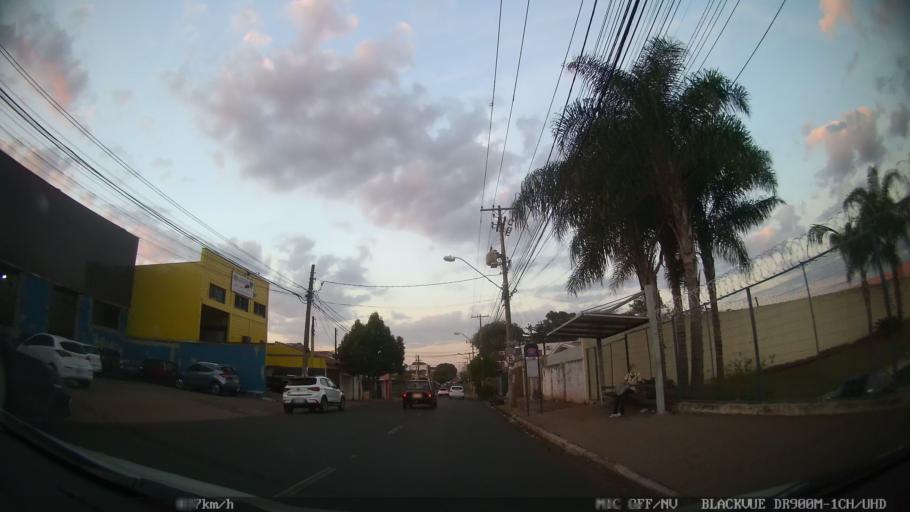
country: BR
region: Sao Paulo
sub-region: Ribeirao Preto
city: Ribeirao Preto
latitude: -21.1497
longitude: -47.8229
